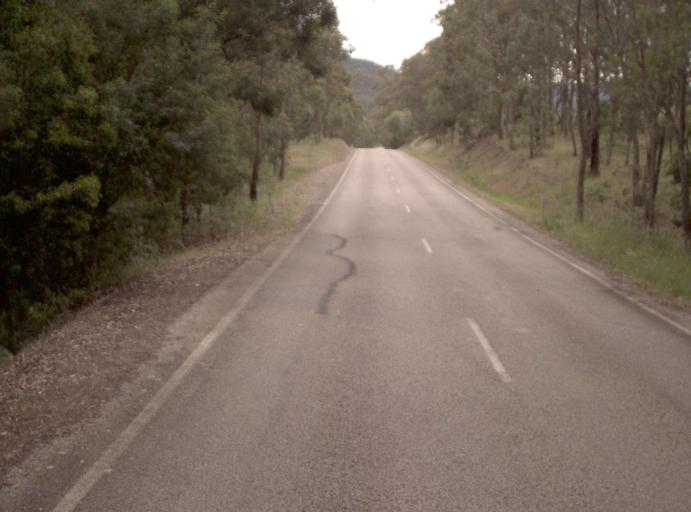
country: AU
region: Victoria
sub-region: East Gippsland
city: Bairnsdale
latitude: -37.5535
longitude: 147.1978
